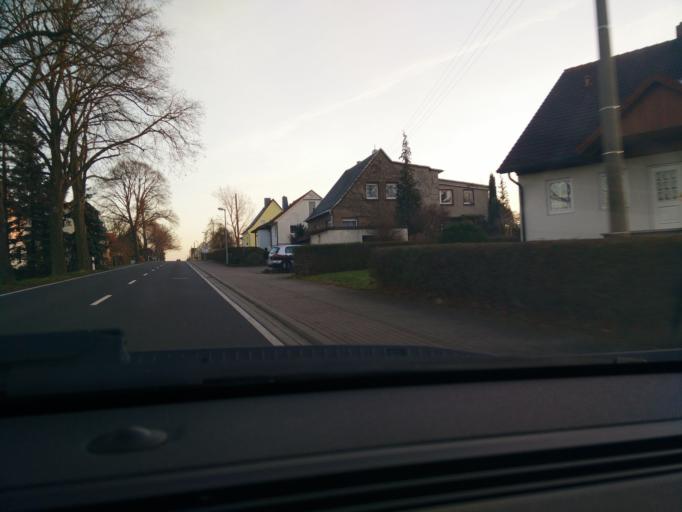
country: DE
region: Saxony
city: Bad Lausick
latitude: 51.1278
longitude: 12.6590
